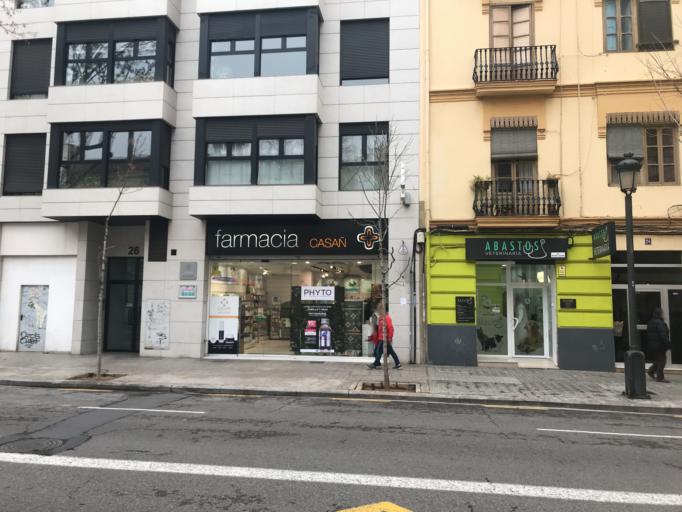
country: ES
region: Valencia
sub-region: Provincia de Valencia
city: Valencia
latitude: 39.4683
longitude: -0.3850
